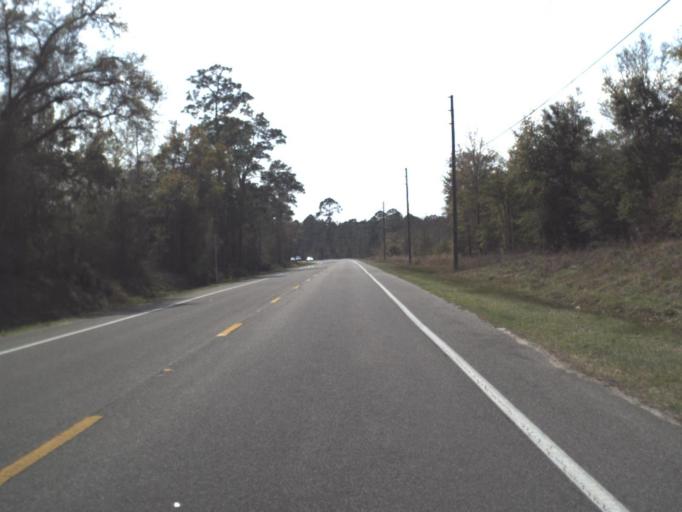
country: US
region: Florida
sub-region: Wakulla County
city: Crawfordville
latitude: 30.0674
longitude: -84.4610
